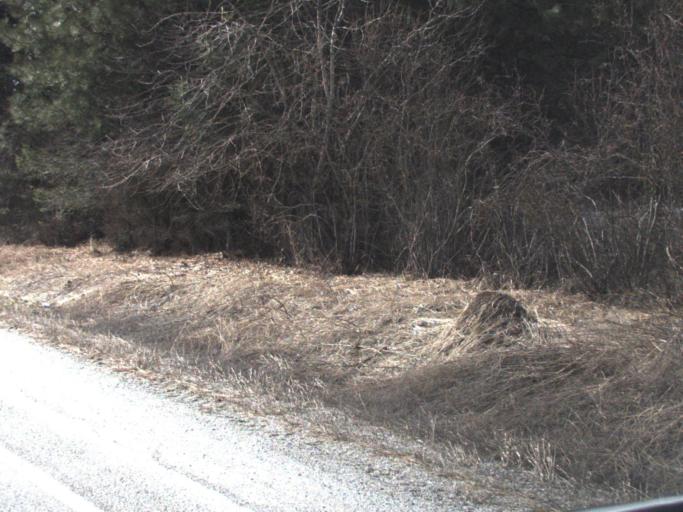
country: US
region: Washington
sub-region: Pend Oreille County
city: Newport
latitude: 48.4906
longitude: -117.2689
